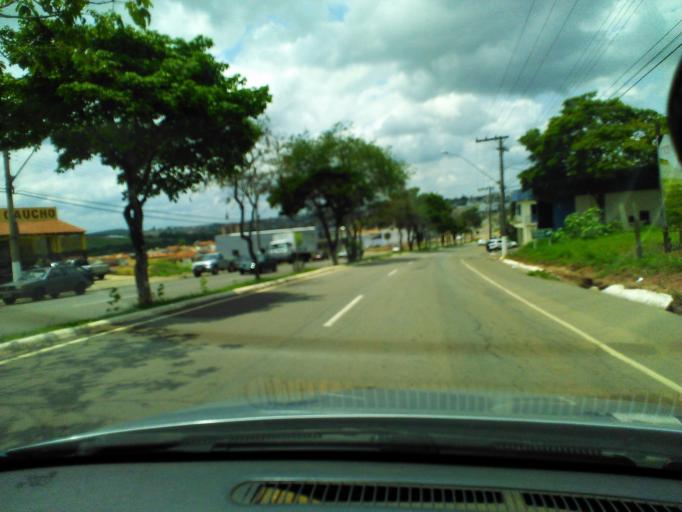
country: BR
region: Minas Gerais
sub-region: Tres Coracoes
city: Tres Coracoes
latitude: -21.6741
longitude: -45.2710
